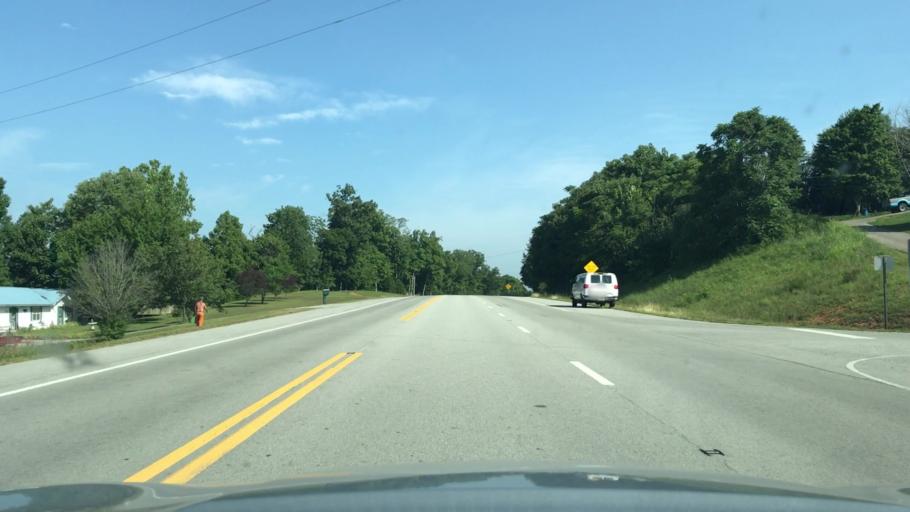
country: US
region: Tennessee
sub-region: Pickett County
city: Byrdstown
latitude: 36.5488
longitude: -85.1657
